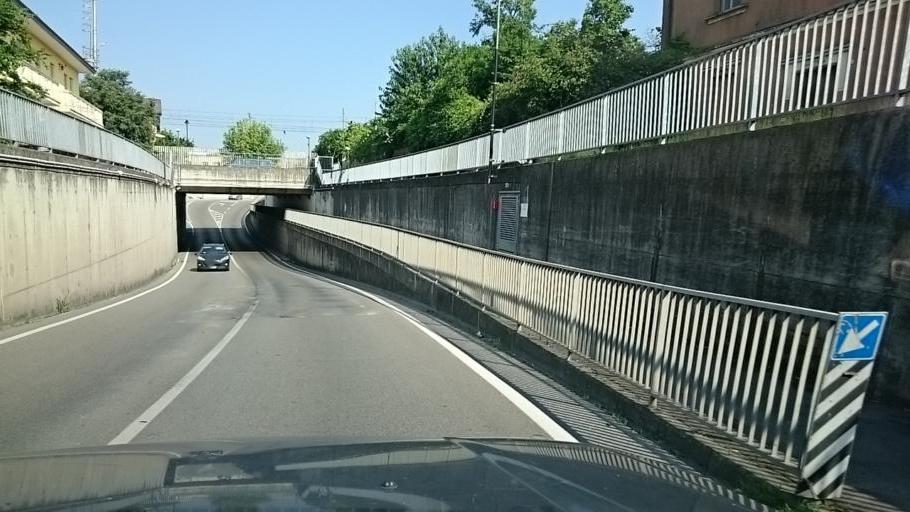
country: IT
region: Veneto
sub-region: Provincia di Padova
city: Vigodarzere
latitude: 45.4522
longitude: 11.8902
